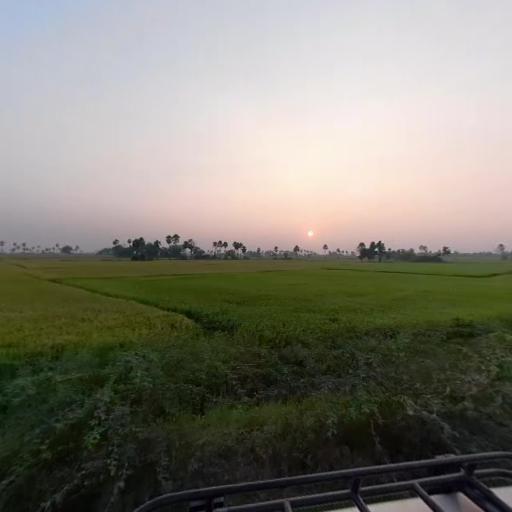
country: IN
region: Telangana
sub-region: Nalgonda
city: Suriapet
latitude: 17.0665
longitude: 79.5477
